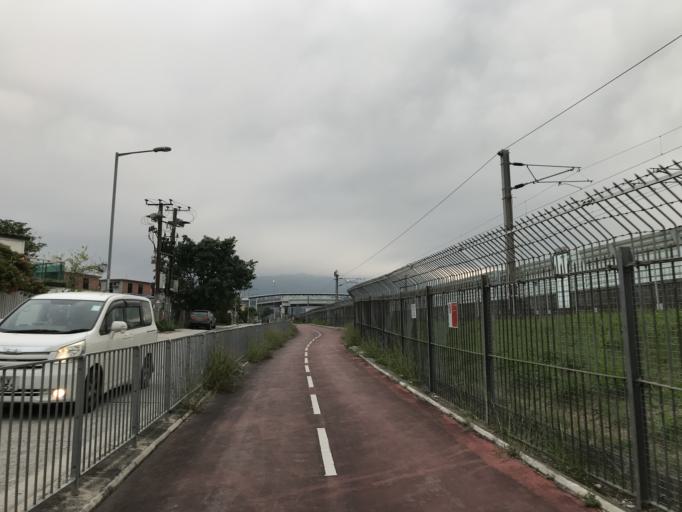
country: HK
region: Tai Po
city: Tai Po
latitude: 22.4774
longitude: 114.1549
